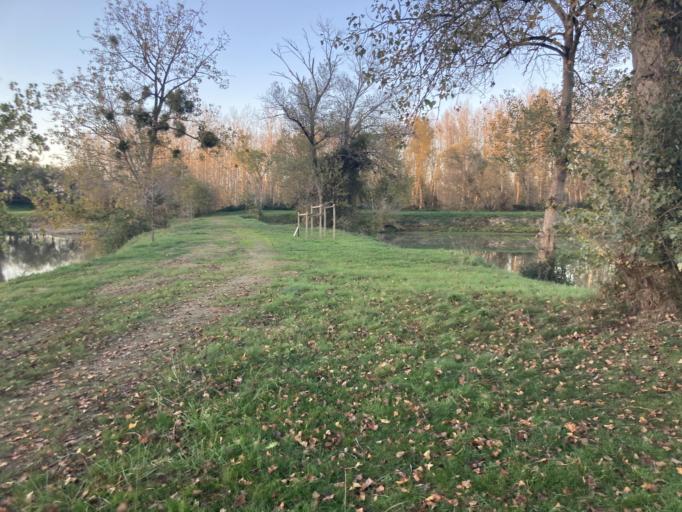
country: FR
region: Aquitaine
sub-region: Departement des Landes
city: Mugron
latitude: 43.7586
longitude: -0.7296
